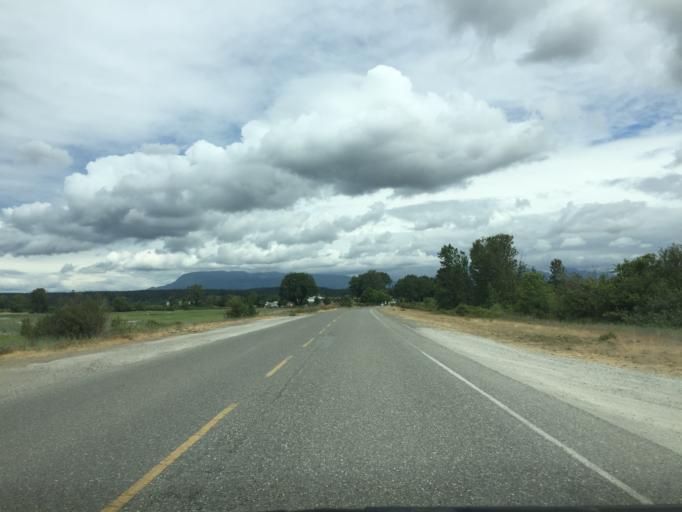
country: CA
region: British Columbia
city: Richmond
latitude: 49.2117
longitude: -123.2026
